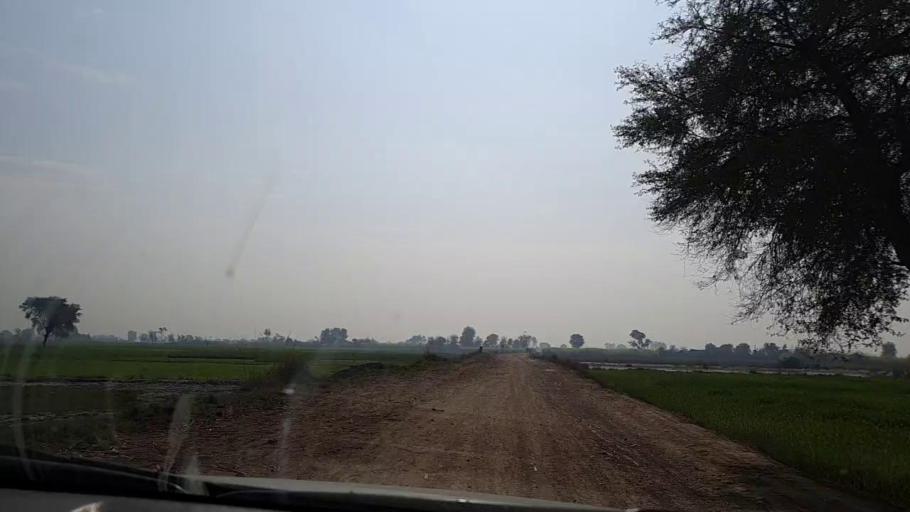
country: PK
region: Sindh
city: Daulatpur
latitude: 26.5428
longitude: 67.9873
